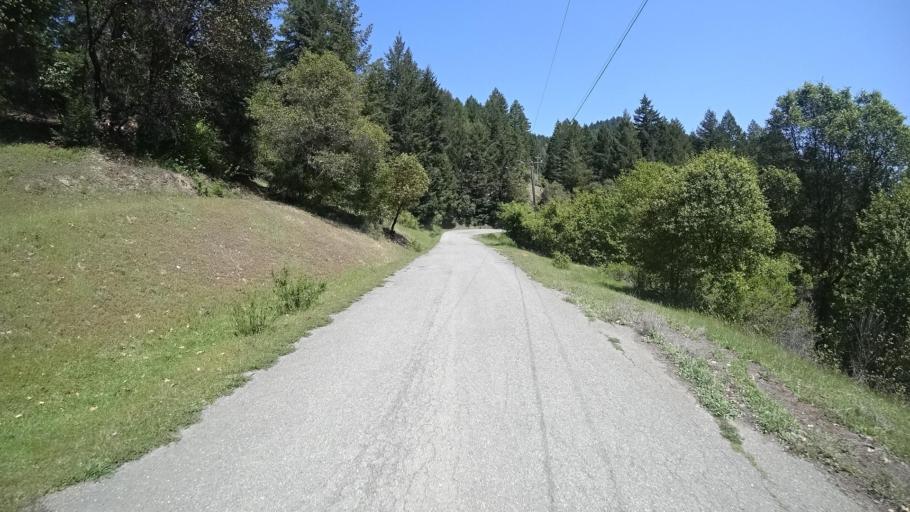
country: US
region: California
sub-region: Humboldt County
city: Redway
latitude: 40.1939
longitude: -123.5609
